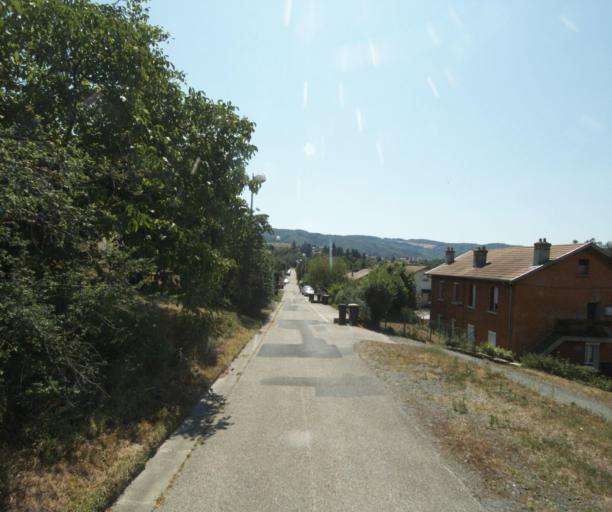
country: FR
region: Rhone-Alpes
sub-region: Departement du Rhone
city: Sain-Bel
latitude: 45.8021
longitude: 4.6082
